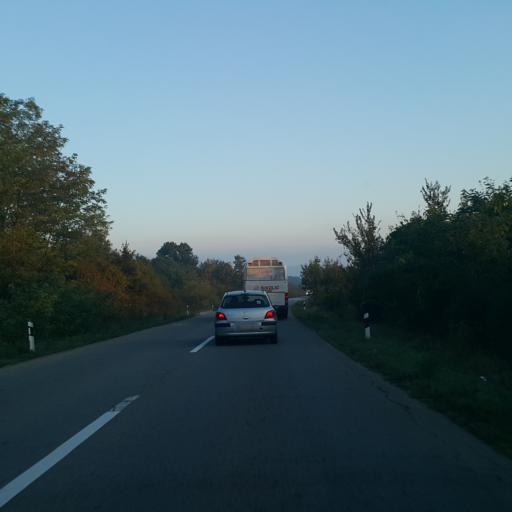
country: RS
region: Central Serbia
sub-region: Zajecarski Okrug
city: Zajecar
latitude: 43.9677
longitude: 22.2944
